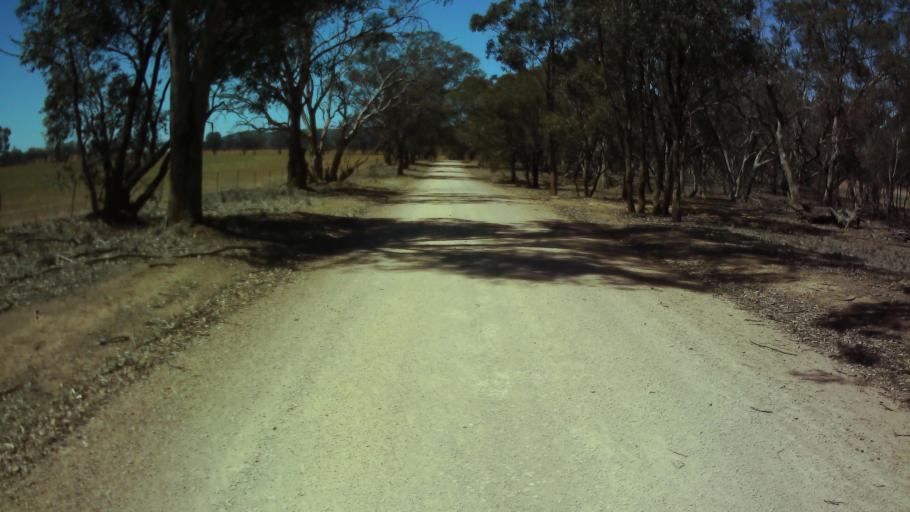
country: AU
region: New South Wales
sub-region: Weddin
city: Grenfell
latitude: -33.9260
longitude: 148.0782
